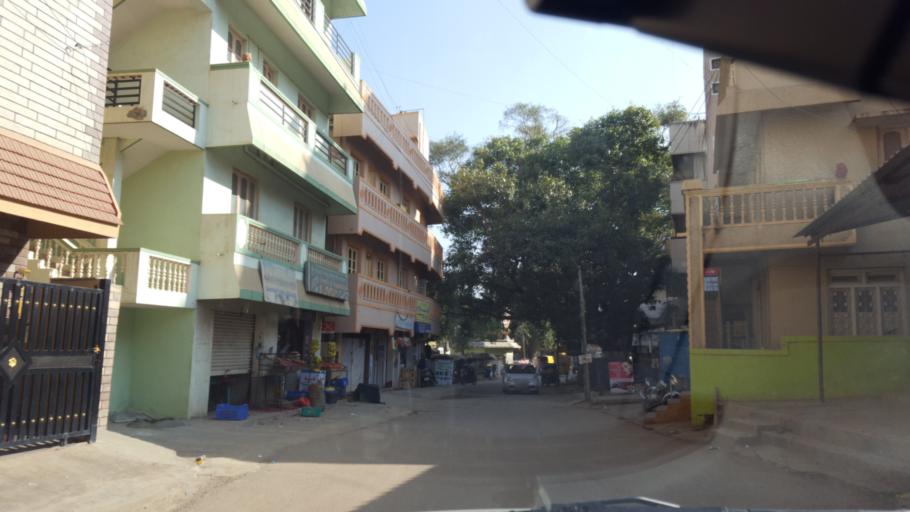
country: IN
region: Karnataka
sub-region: Bangalore Urban
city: Bangalore
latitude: 12.9493
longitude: 77.7078
